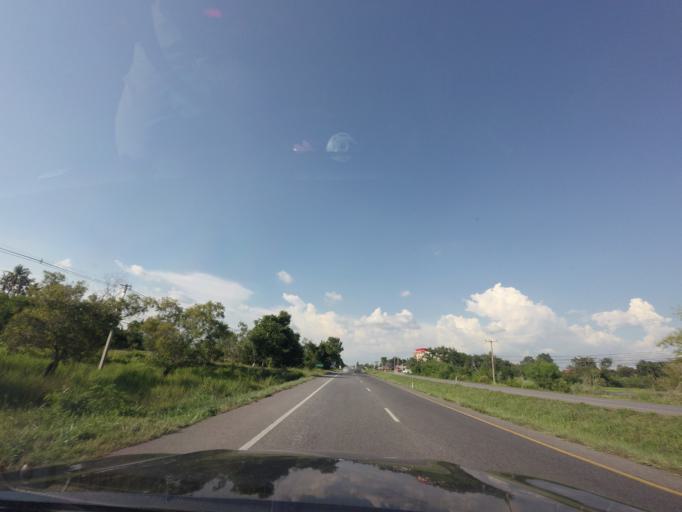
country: TH
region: Khon Kaen
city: Non Sila
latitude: 15.9963
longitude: 102.7005
